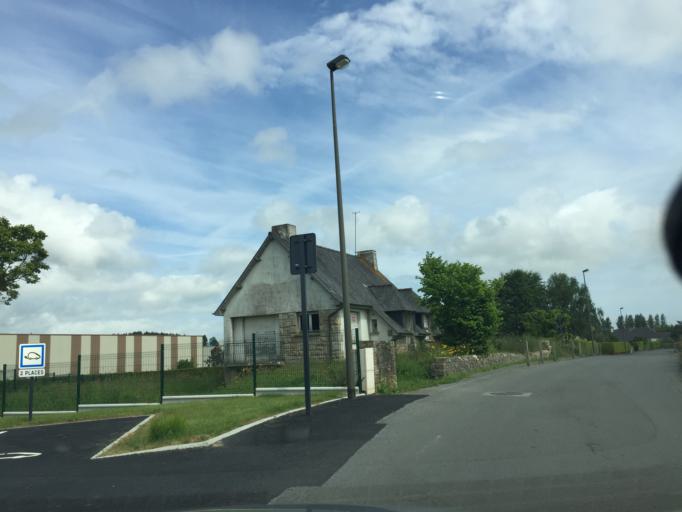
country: FR
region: Brittany
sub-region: Departement des Cotes-d'Armor
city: Corseul
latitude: 48.5128
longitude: -2.1265
